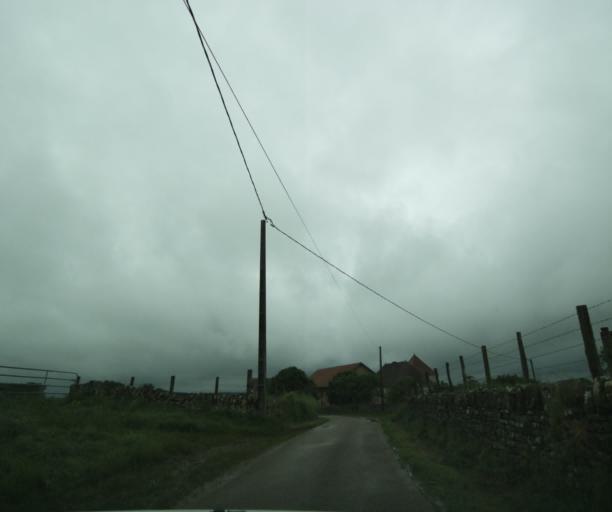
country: FR
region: Bourgogne
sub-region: Departement de Saone-et-Loire
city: Charolles
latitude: 46.3824
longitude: 4.2288
